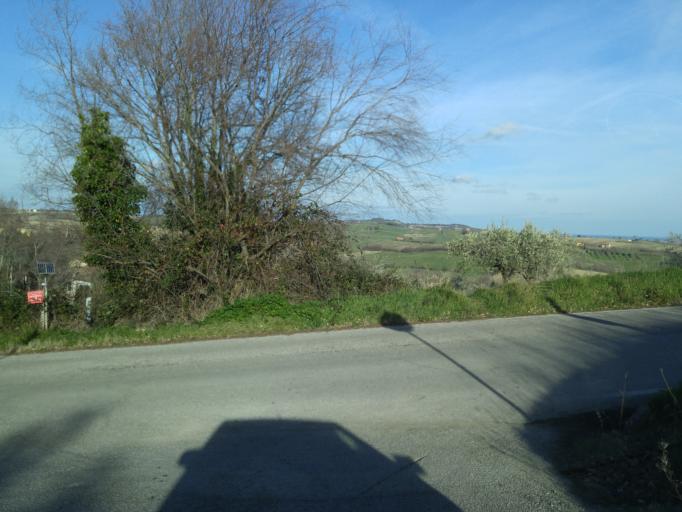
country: IT
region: The Marches
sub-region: Provincia di Pesaro e Urbino
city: Cartoceto
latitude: 43.7776
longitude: 12.8955
